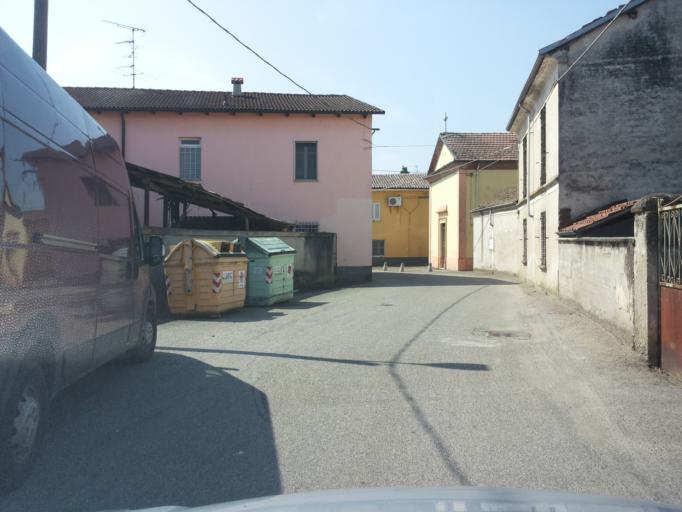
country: IT
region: Lombardy
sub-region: Provincia di Pavia
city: Palestro
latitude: 45.2693
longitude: 8.5358
